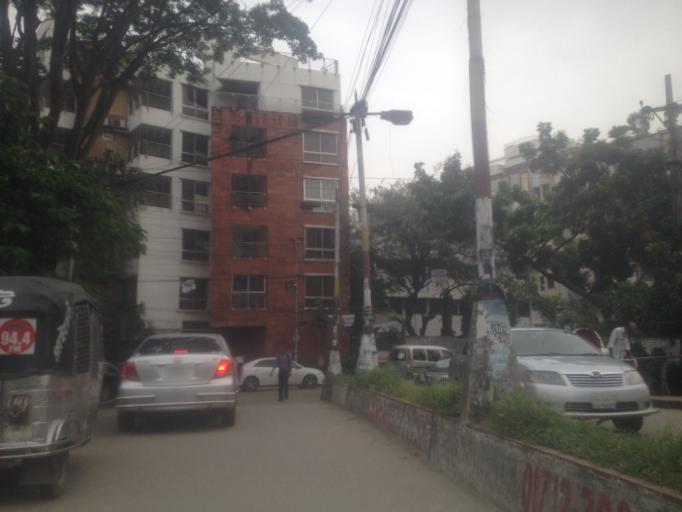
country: BD
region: Dhaka
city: Azimpur
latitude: 23.7510
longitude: 90.3736
